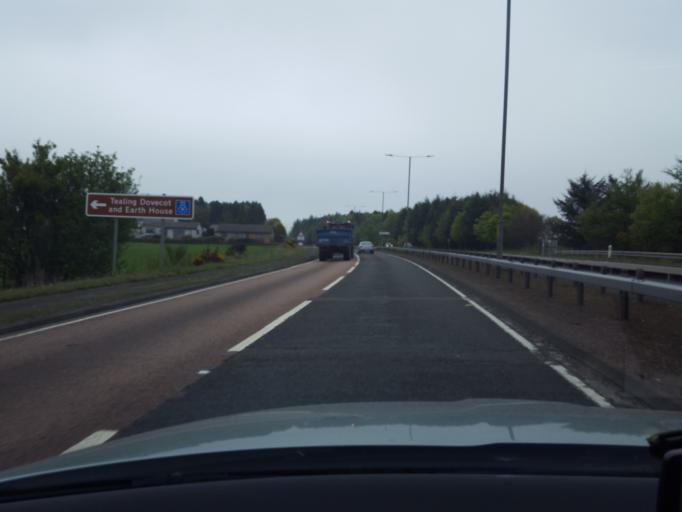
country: GB
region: Scotland
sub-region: Dundee City
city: Dundee
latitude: 56.5266
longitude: -2.9445
